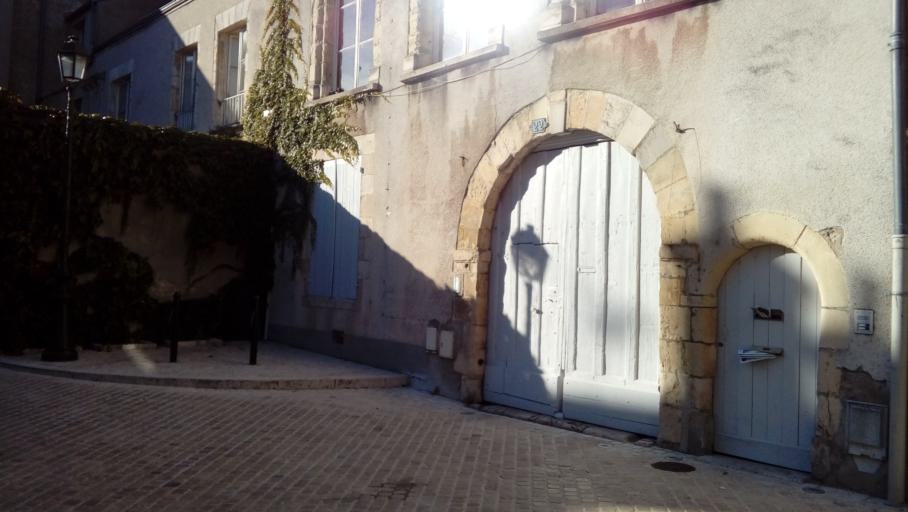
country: FR
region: Centre
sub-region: Departement du Loiret
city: Orleans
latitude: 47.9013
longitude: 1.9122
